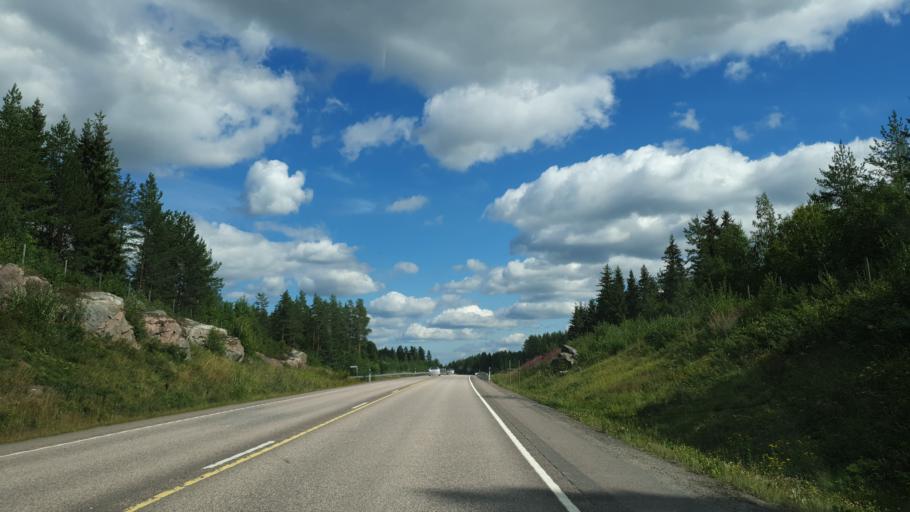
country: FI
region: Pirkanmaa
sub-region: Tampere
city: Kuhmalahti
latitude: 61.7093
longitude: 24.6101
